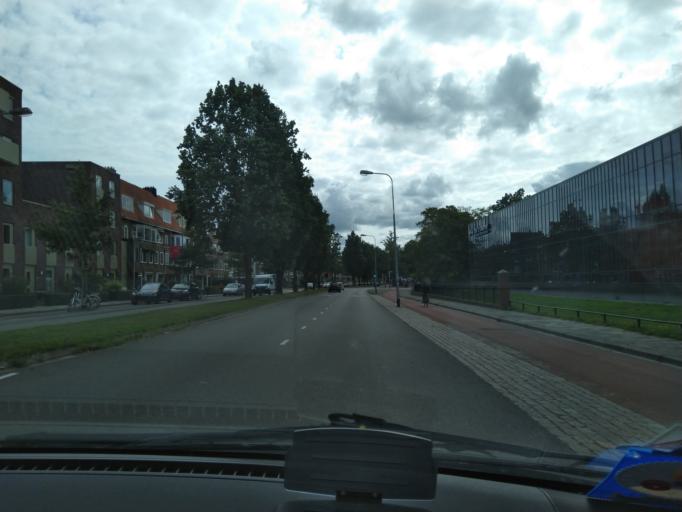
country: NL
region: Groningen
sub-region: Gemeente Groningen
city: Groningen
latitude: 53.2078
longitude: 6.5577
